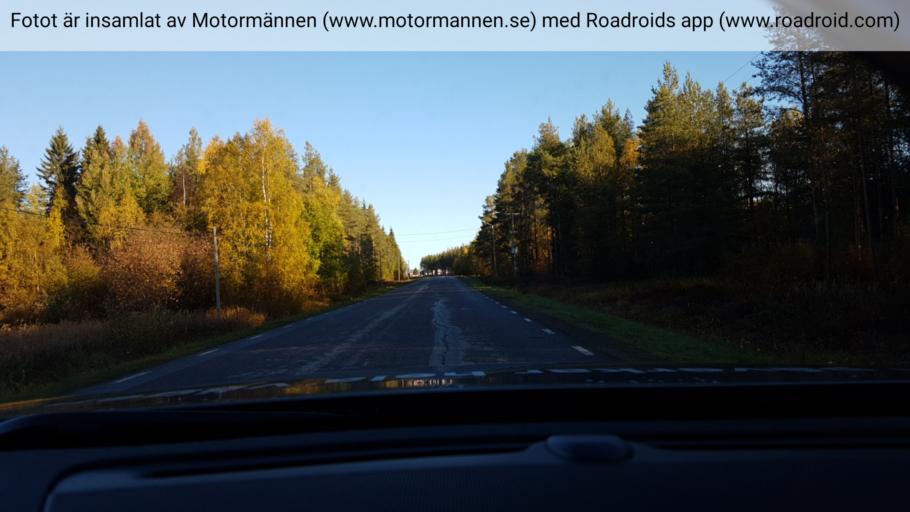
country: SE
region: Norrbotten
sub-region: Bodens Kommun
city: Boden
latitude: 65.8873
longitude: 21.6777
